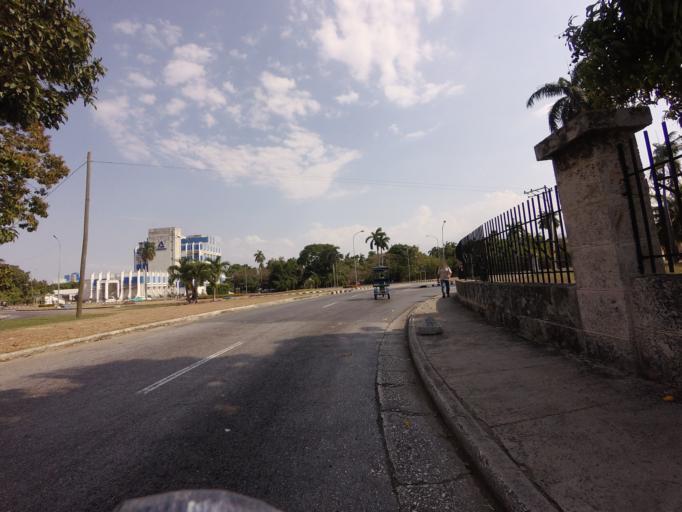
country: CU
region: La Habana
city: Cerro
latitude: 23.0763
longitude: -82.4573
